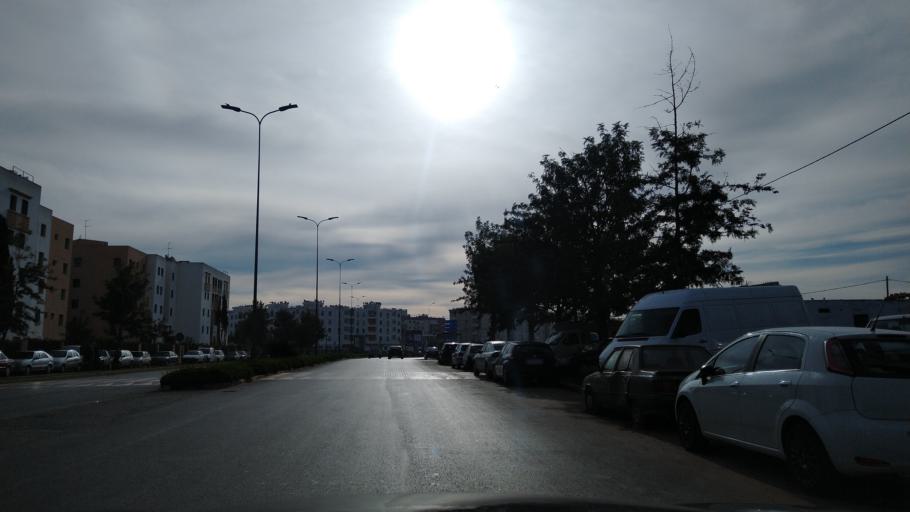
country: MA
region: Rabat-Sale-Zemmour-Zaer
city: Sale
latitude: 33.9899
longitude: -6.7406
